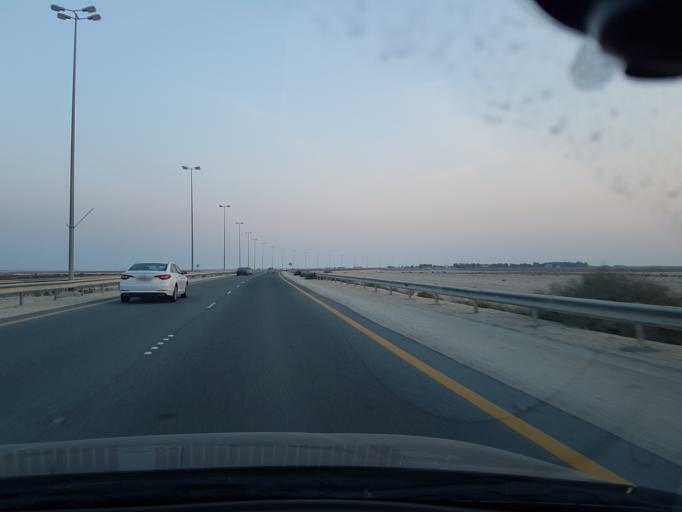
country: BH
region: Central Governorate
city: Dar Kulayb
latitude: 26.0030
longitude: 50.4850
